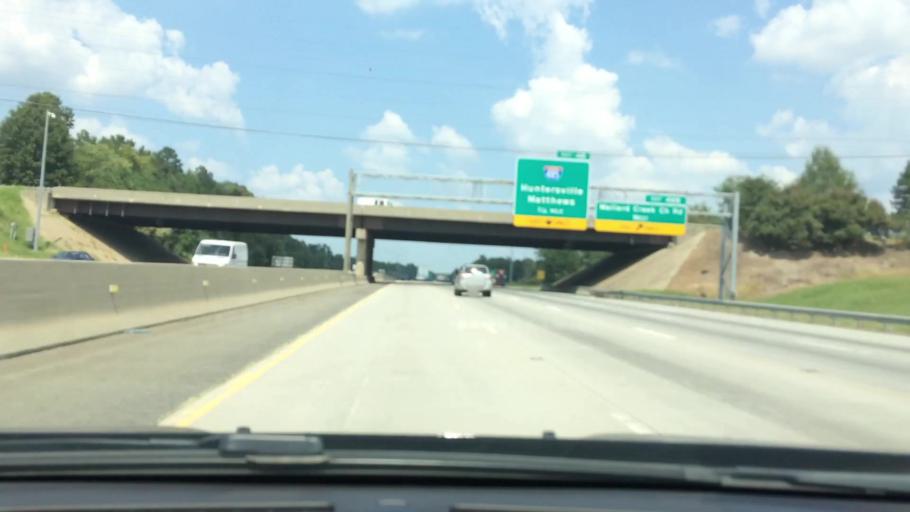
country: US
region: North Carolina
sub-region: Cabarrus County
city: Harrisburg
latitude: 35.3313
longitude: -80.7445
